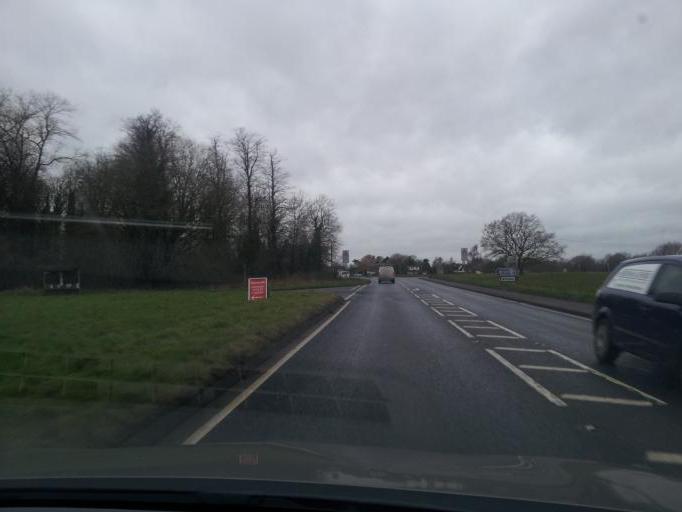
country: GB
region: England
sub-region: Norfolk
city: Diss
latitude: 52.3530
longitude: 1.0594
